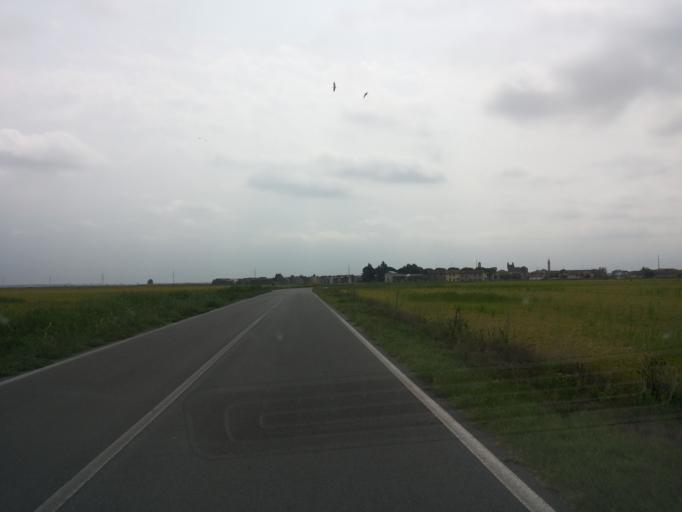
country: IT
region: Piedmont
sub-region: Provincia di Vercelli
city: Prarolo
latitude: 45.2886
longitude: 8.4754
